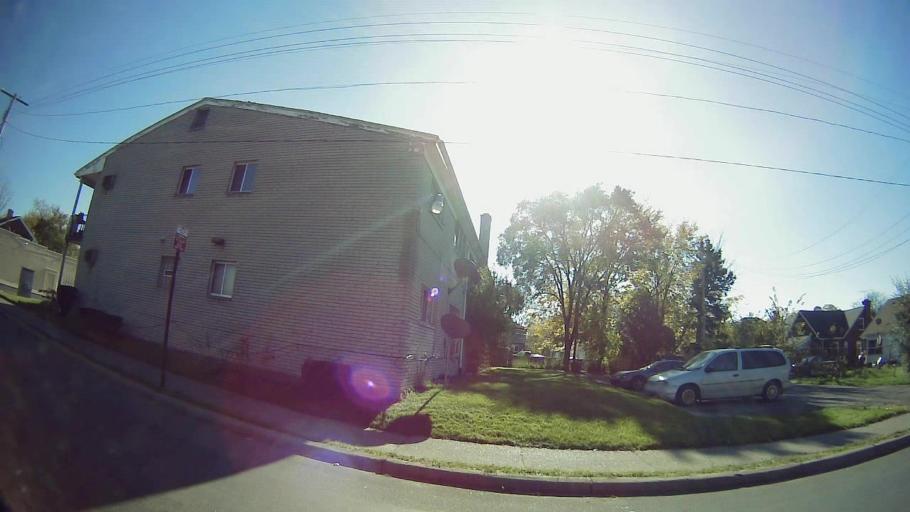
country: US
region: Michigan
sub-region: Oakland County
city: Oak Park
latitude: 42.4013
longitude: -83.2070
